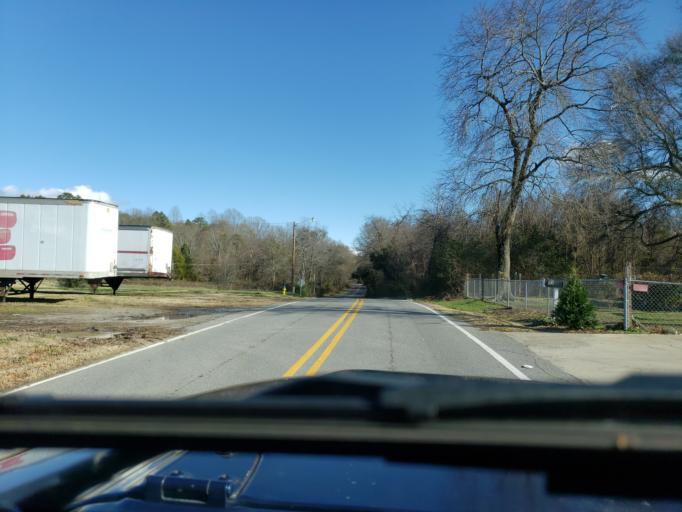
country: US
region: North Carolina
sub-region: Cleveland County
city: White Plains
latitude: 35.1725
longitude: -81.4426
